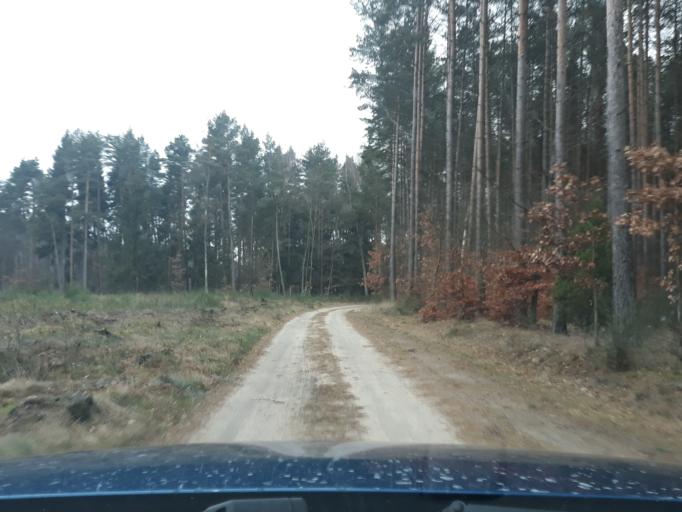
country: PL
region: Pomeranian Voivodeship
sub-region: Powiat czluchowski
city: Czluchow
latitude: 53.8196
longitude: 17.4267
